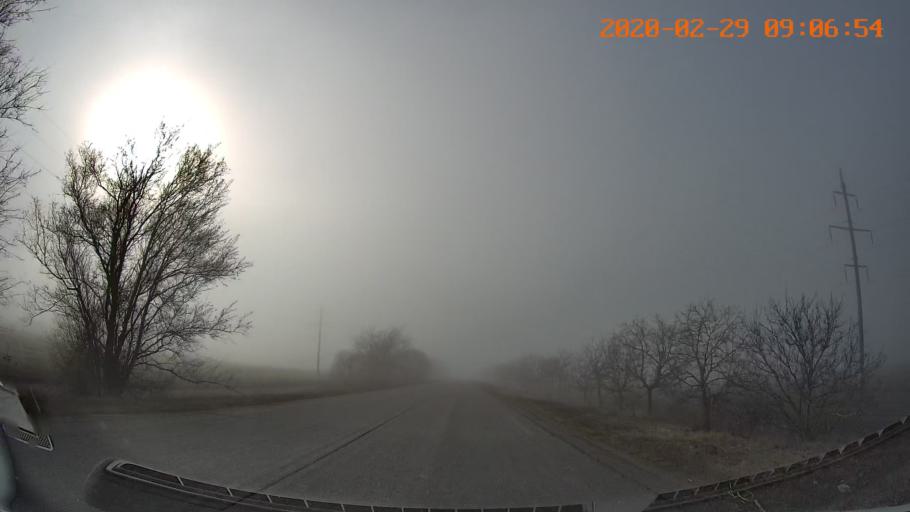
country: MD
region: Telenesti
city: Tiraspolul Nou
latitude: 46.8694
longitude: 29.7466
